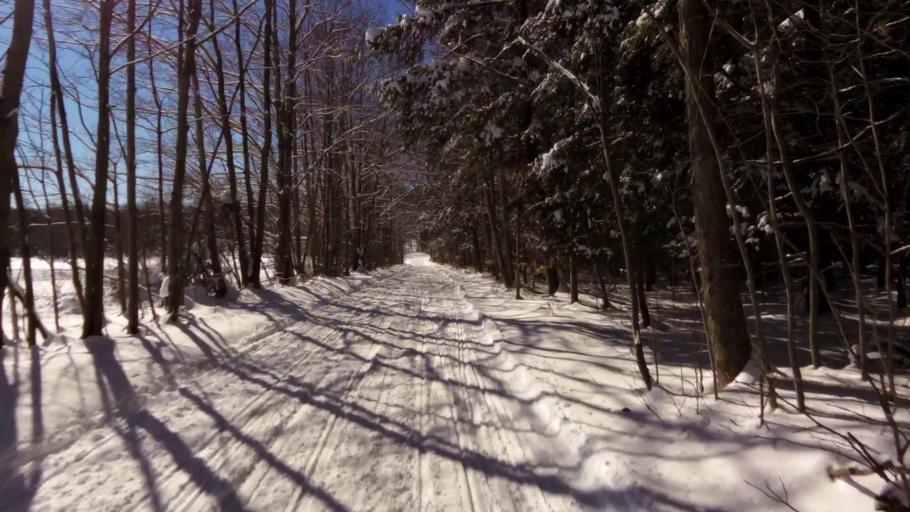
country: US
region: New York
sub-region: Chautauqua County
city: Mayville
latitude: 42.2359
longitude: -79.5198
